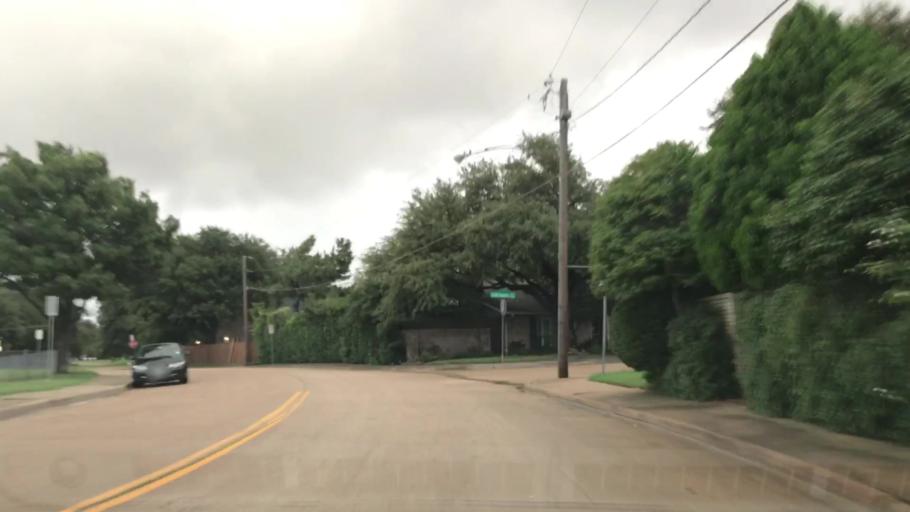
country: US
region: Texas
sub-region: Dallas County
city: University Park
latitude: 32.8820
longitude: -96.7839
